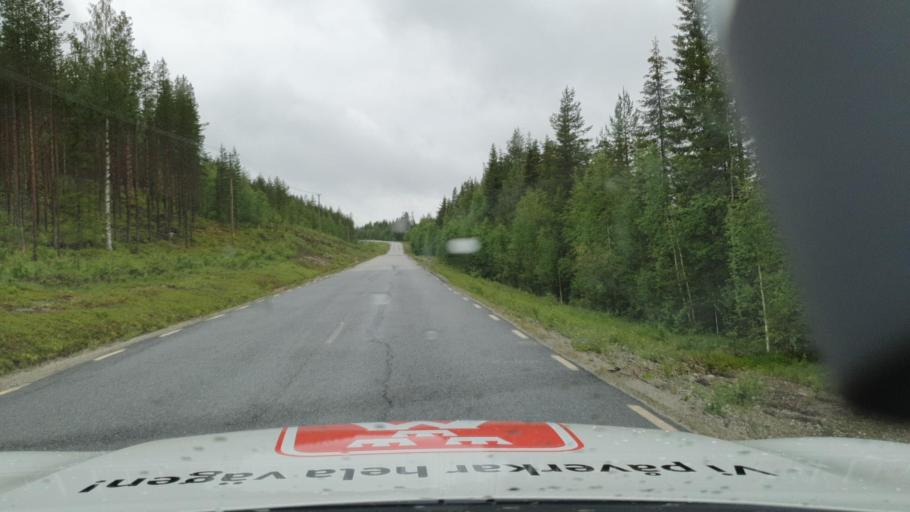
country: SE
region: Vaesterbotten
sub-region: Asele Kommun
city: Asele
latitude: 64.0062
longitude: 17.2148
